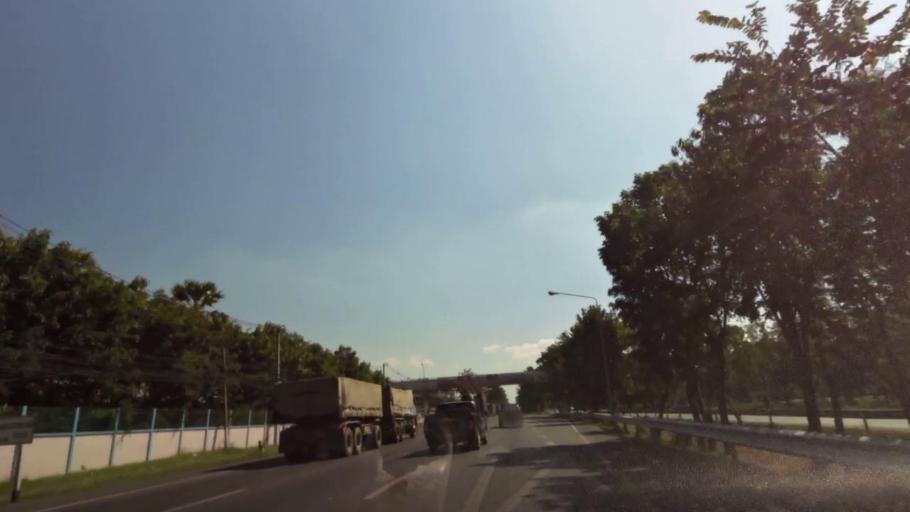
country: TH
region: Nakhon Sawan
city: Nakhon Sawan
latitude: 15.6653
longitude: 100.1289
